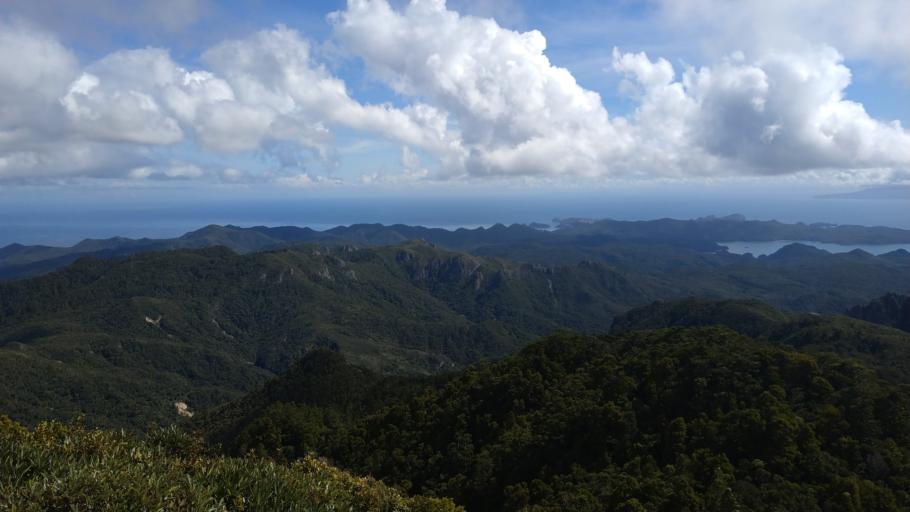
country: NZ
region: Waikato
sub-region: Thames-Coromandel District
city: Coromandel
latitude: -36.1860
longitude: 175.4128
